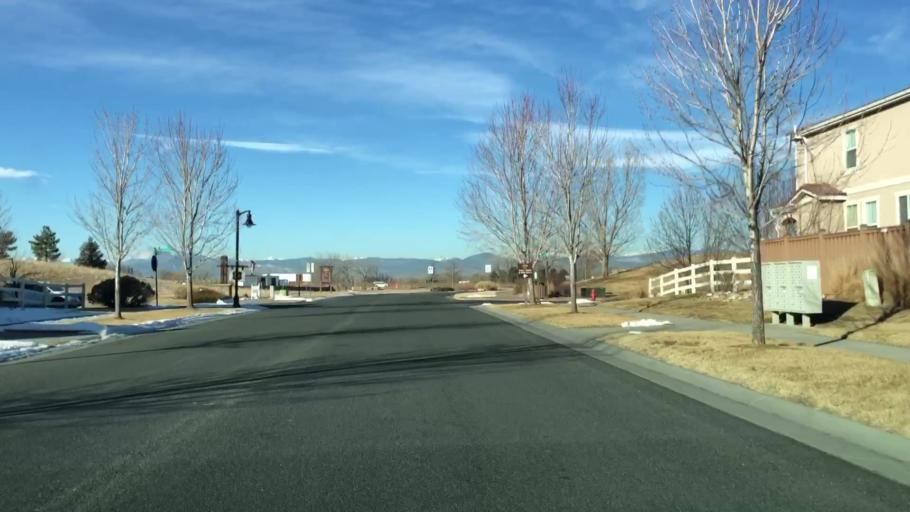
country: US
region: Colorado
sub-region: Larimer County
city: Loveland
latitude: 40.3907
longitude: -104.9895
